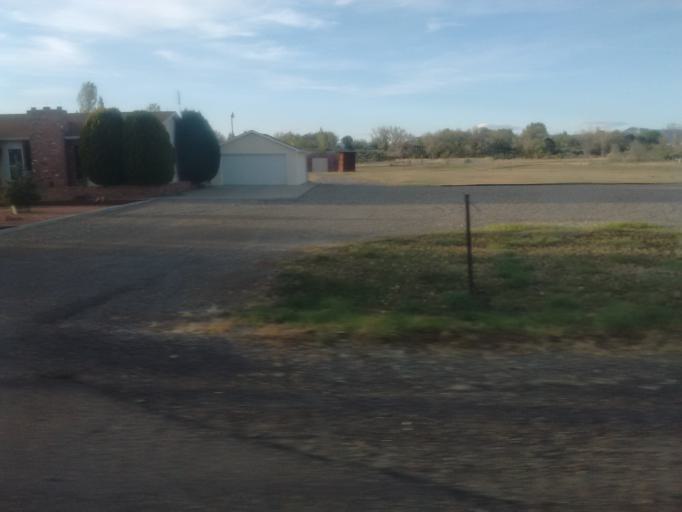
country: US
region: Colorado
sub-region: Mesa County
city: Grand Junction
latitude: 39.1064
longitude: -108.5867
